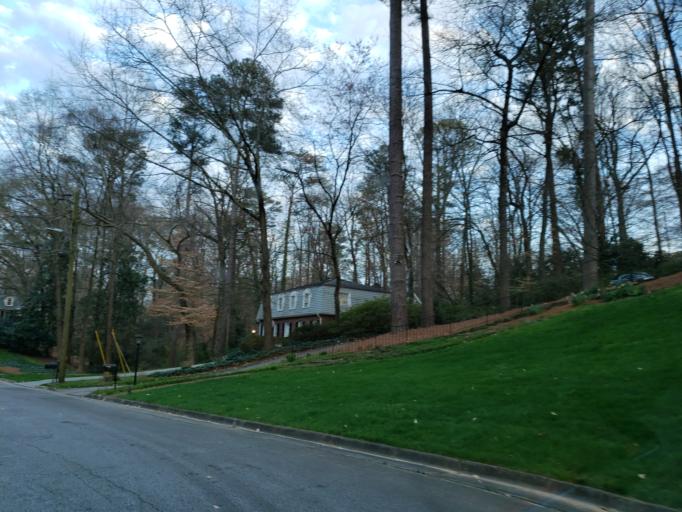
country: US
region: Georgia
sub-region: Cobb County
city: Vinings
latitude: 33.8252
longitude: -84.4013
